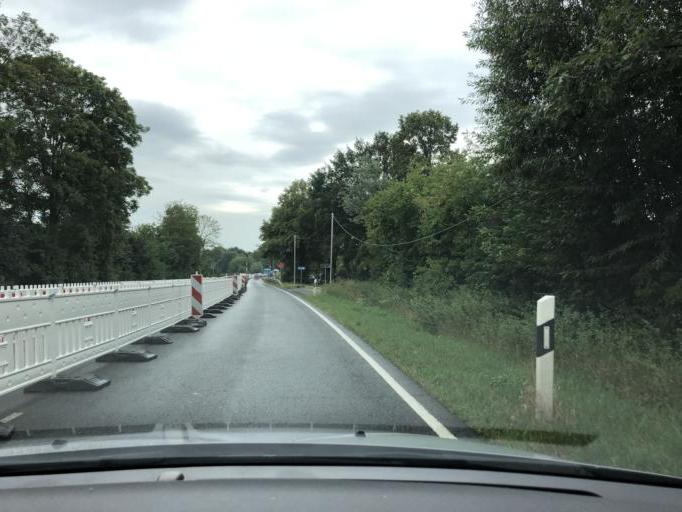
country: DE
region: North Rhine-Westphalia
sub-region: Regierungsbezirk Dusseldorf
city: Schermbeck
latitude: 51.6760
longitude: 6.8604
